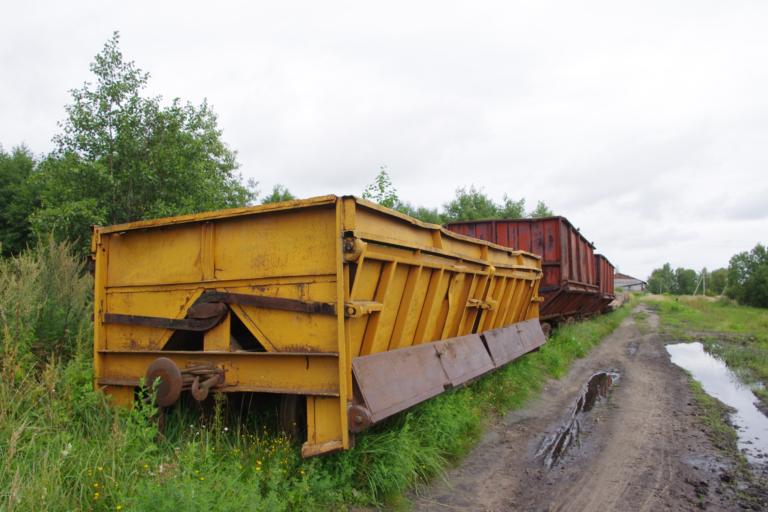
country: BY
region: Vitebsk
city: Chashniki
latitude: 55.3403
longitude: 29.3093
